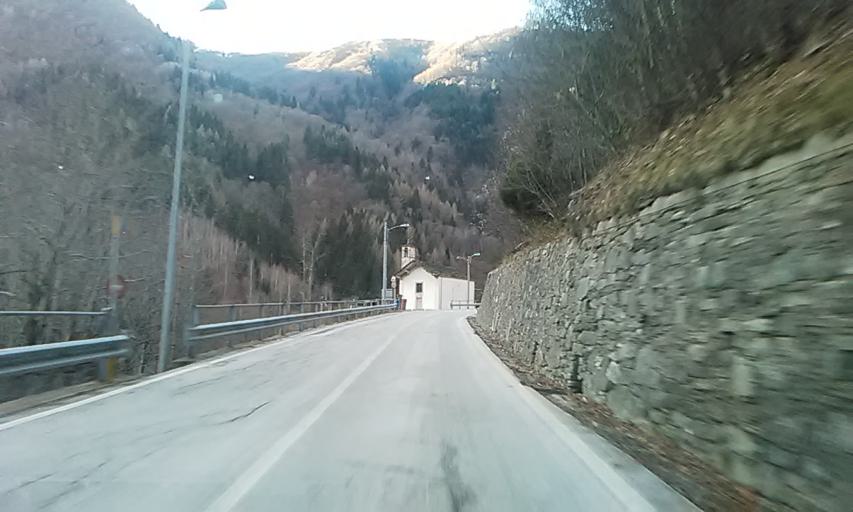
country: IT
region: Piedmont
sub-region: Provincia di Vercelli
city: Boccioleto
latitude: 45.8295
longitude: 8.1086
